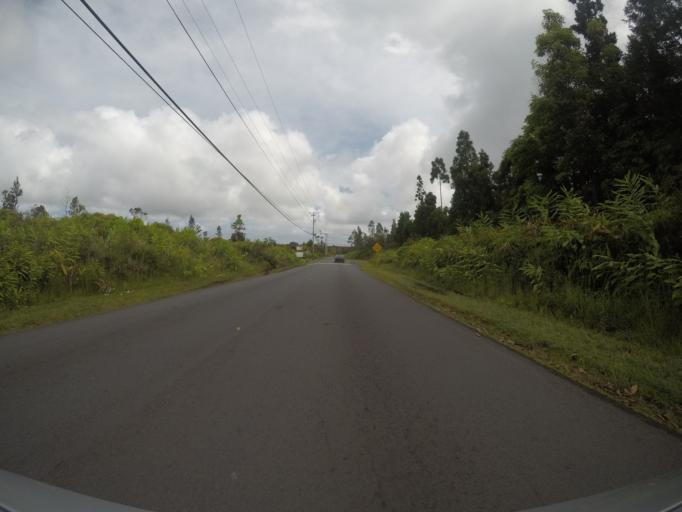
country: US
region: Hawaii
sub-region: Hawaii County
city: Fern Acres
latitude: 19.4776
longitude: -155.1416
